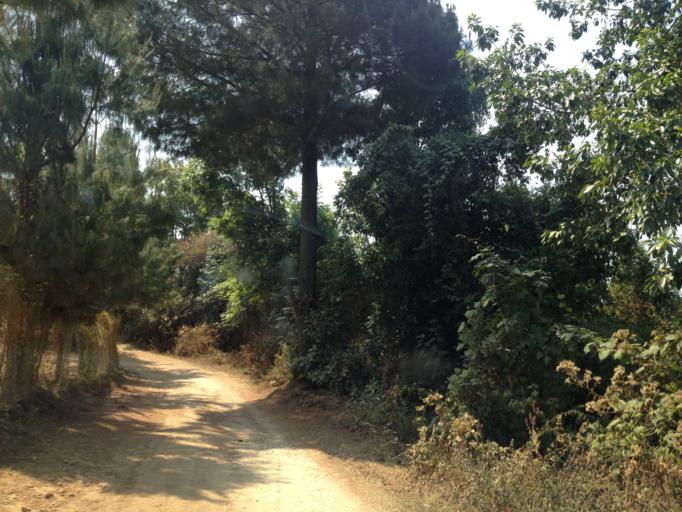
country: MX
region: Michoacan
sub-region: Zitacuaro
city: Macutzio
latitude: 19.4941
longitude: -100.3250
